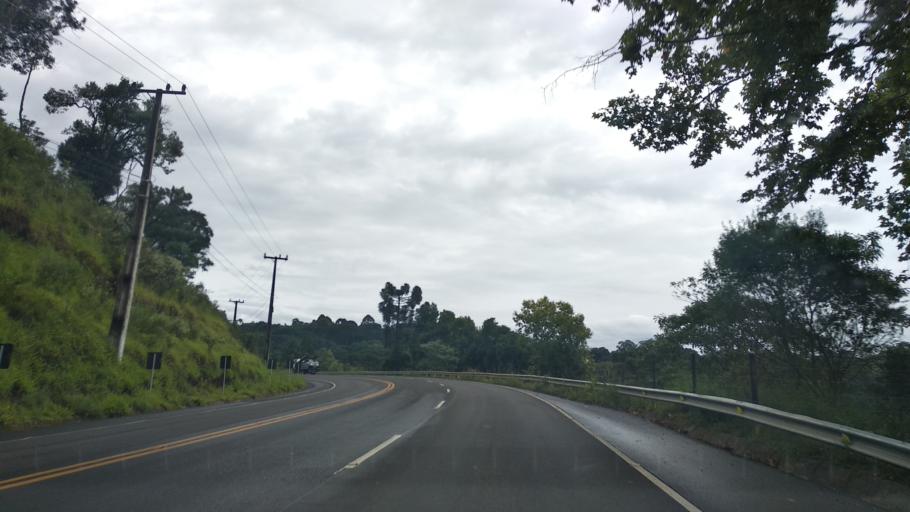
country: BR
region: Santa Catarina
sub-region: Videira
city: Videira
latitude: -27.0524
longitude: -51.1742
